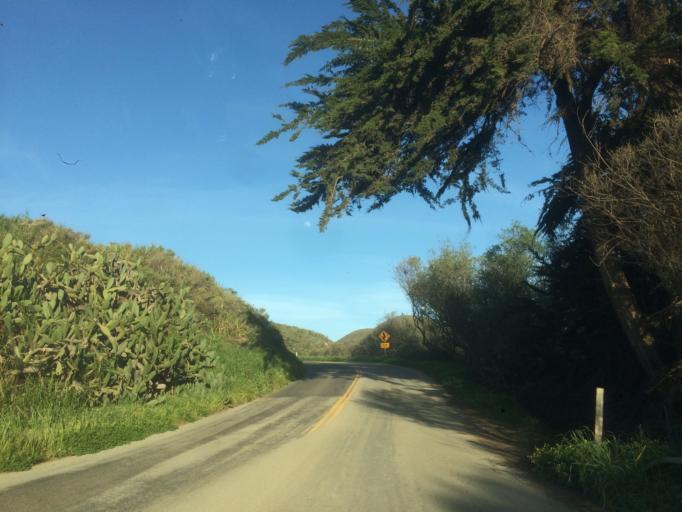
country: US
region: California
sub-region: San Luis Obispo County
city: Los Osos
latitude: 35.2747
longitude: -120.8866
